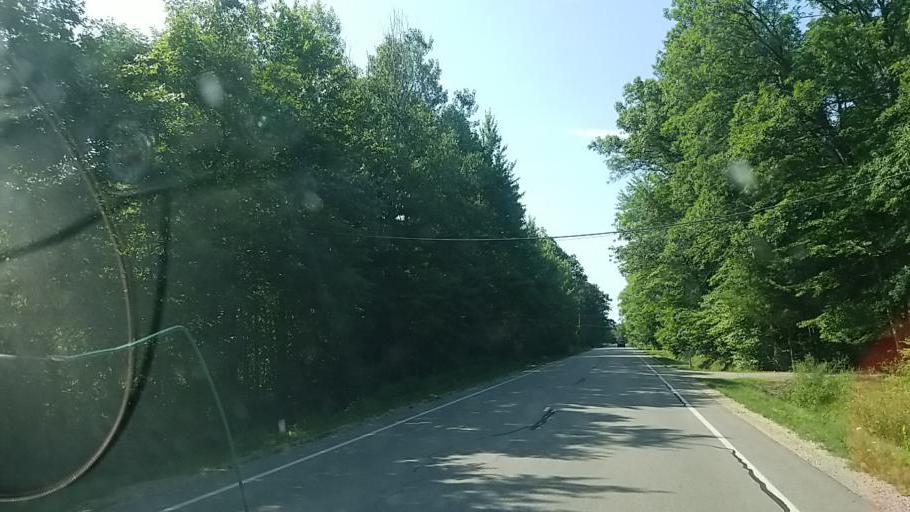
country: US
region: Michigan
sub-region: Muskegon County
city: Whitehall
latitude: 43.3607
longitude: -86.3462
